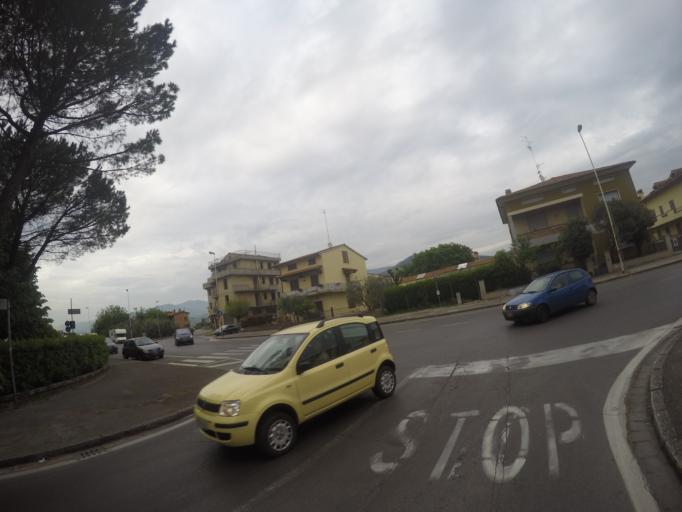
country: IT
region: Tuscany
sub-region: Provincia di Prato
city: Prato
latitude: 43.8973
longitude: 11.0657
